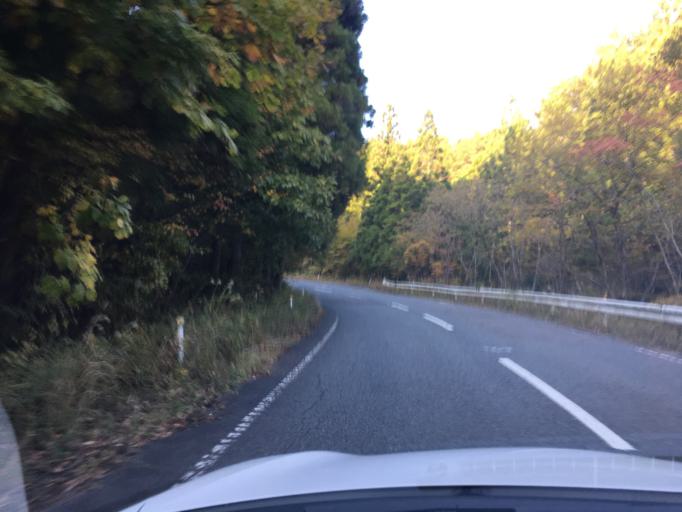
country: JP
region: Fukushima
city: Funehikimachi-funehiki
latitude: 37.2766
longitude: 140.7641
